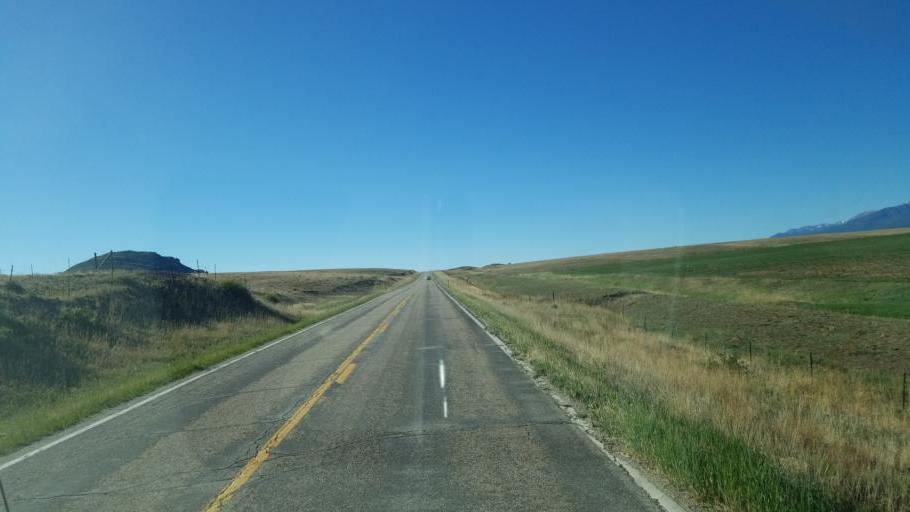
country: US
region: Colorado
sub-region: Custer County
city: Westcliffe
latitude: 38.2123
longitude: -105.5465
